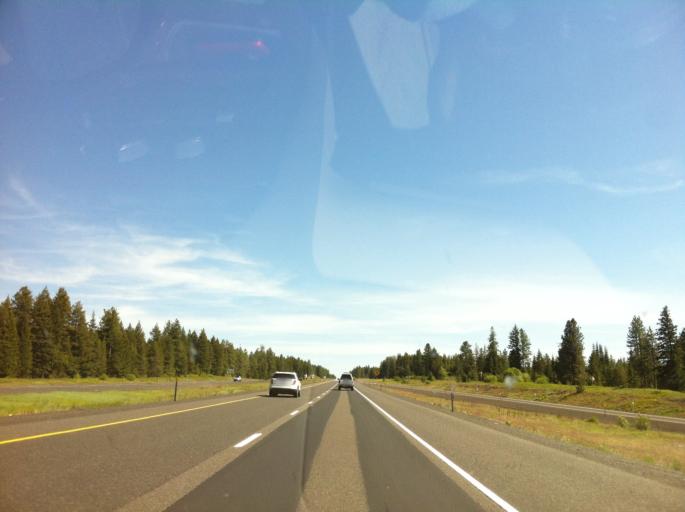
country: US
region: Oregon
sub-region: Umatilla County
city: Mission
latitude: 45.5070
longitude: -118.4266
